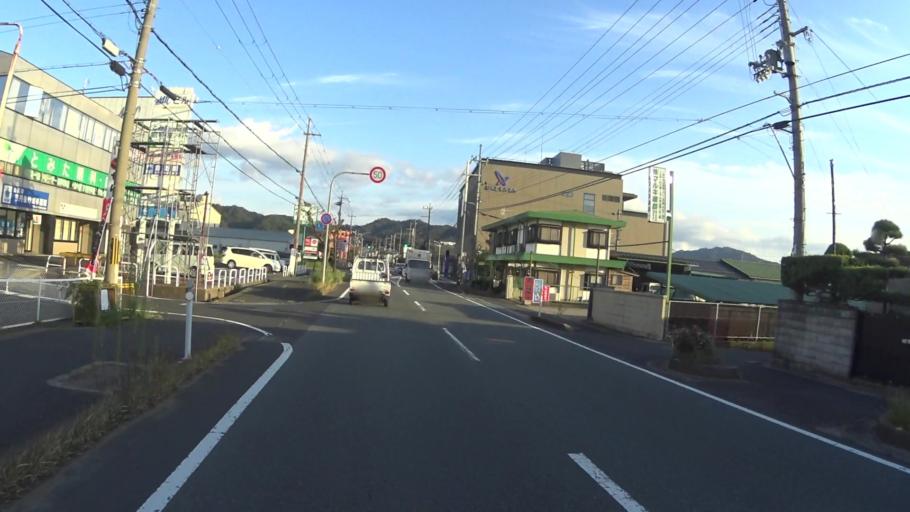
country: JP
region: Kyoto
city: Miyazu
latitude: 35.5881
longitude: 135.0960
